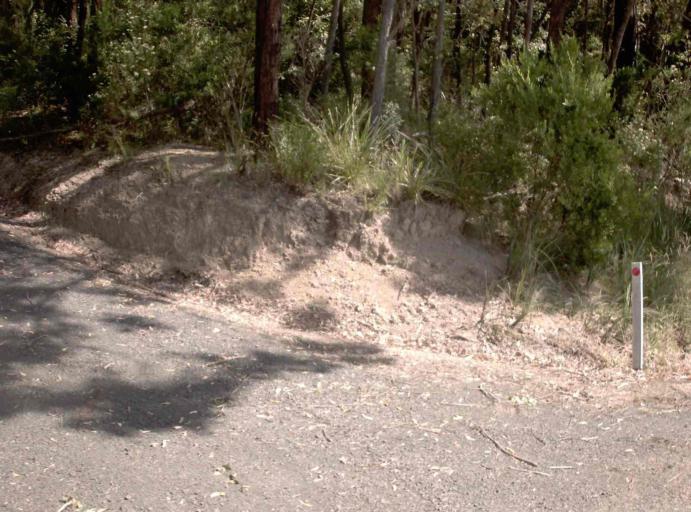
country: AU
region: Victoria
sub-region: Cardinia
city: Bunyip
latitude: -38.2813
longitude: 145.7735
